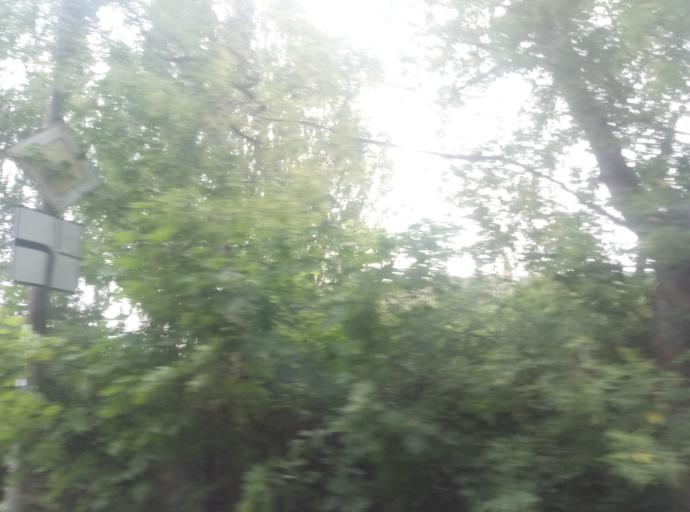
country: RU
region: Tula
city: Bogoroditsk
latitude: 53.7706
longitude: 38.1472
